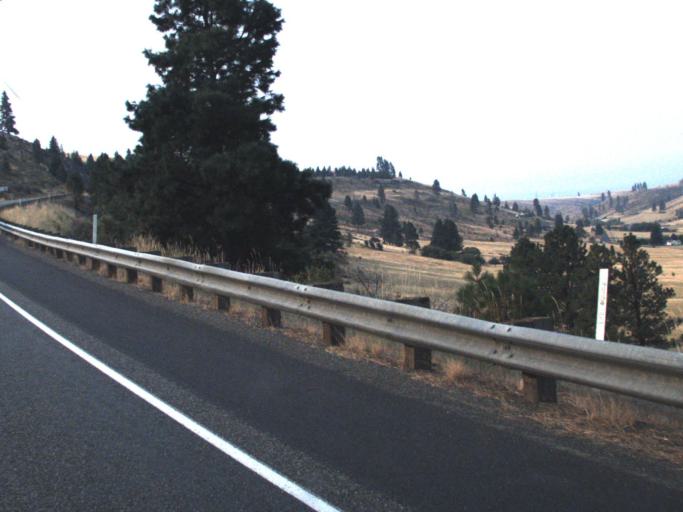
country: US
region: Washington
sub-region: Kittitas County
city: Ellensburg
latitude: 47.1762
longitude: -120.7024
